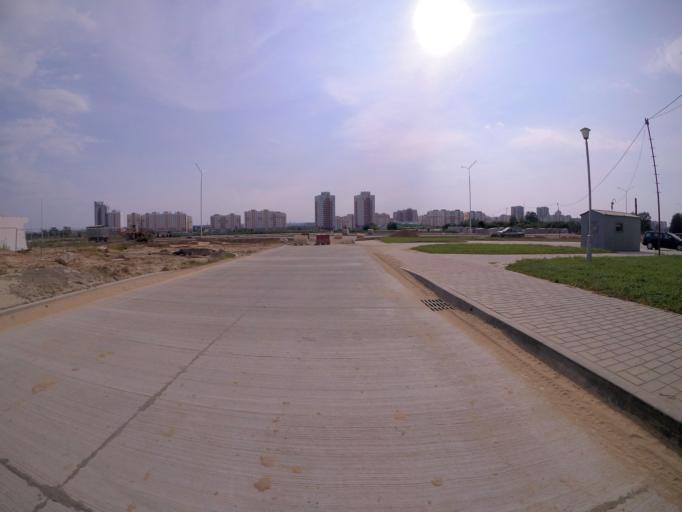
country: BY
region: Grodnenskaya
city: Hrodna
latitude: 53.7174
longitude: 23.8663
